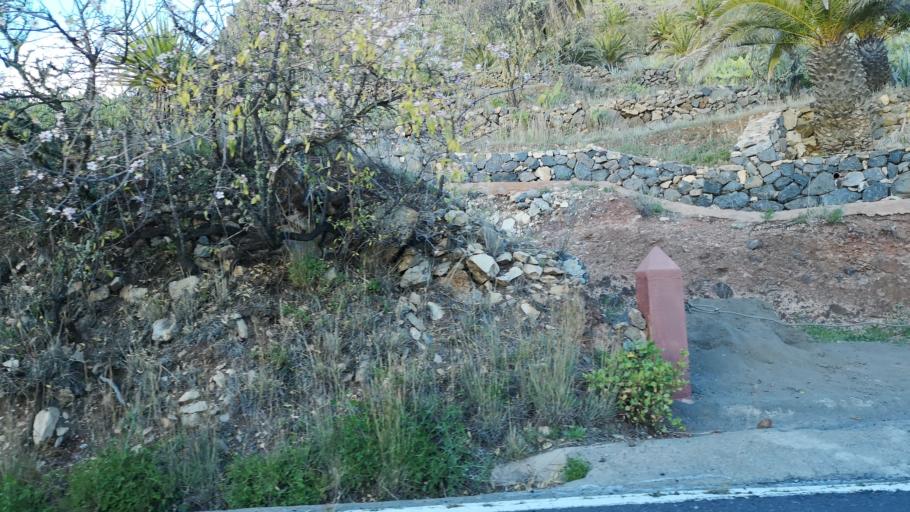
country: ES
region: Canary Islands
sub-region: Provincia de Santa Cruz de Tenerife
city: Alajero
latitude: 28.0737
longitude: -17.2383
